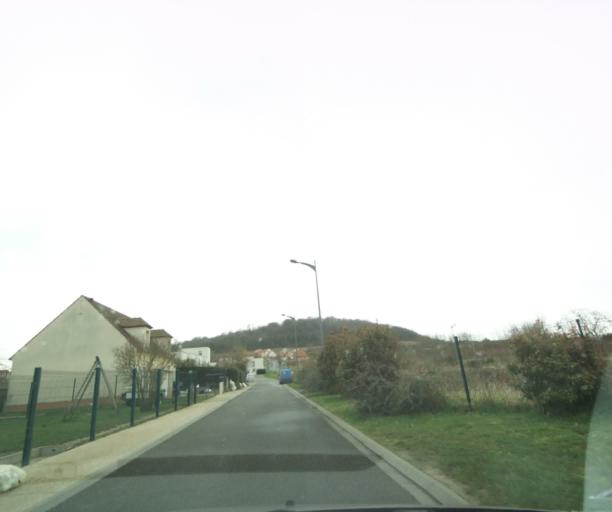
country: FR
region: Picardie
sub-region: Departement de l'Oise
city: Noyon
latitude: 49.5781
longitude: 3.0225
